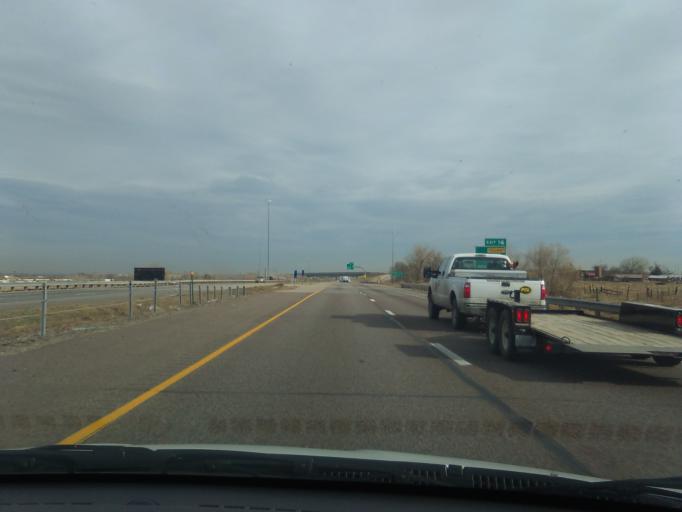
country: US
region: Colorado
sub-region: Adams County
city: Brighton
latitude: 39.9044
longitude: -104.8330
